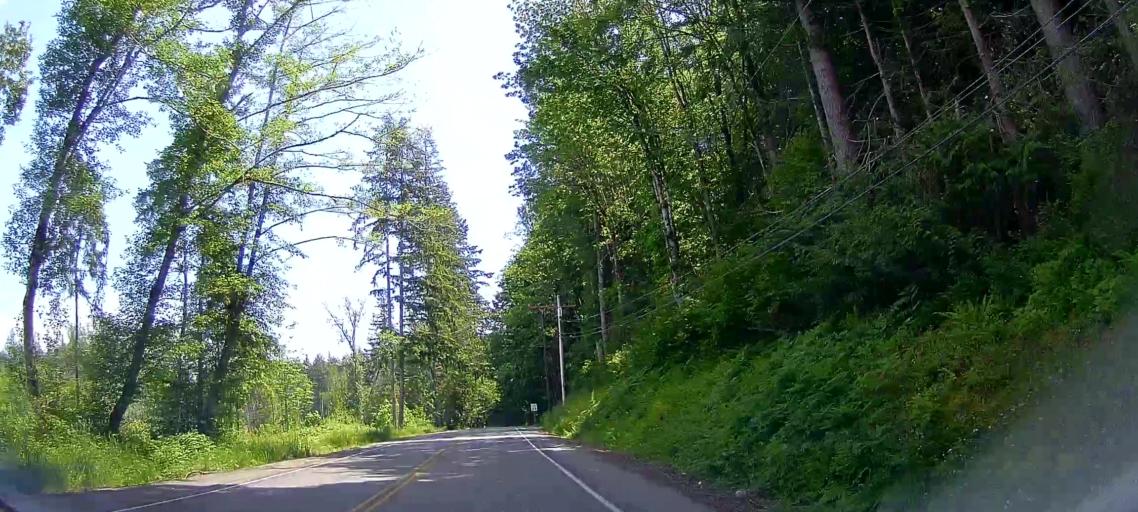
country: US
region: Washington
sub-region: Skagit County
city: Mount Vernon
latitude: 48.4002
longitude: -122.3027
